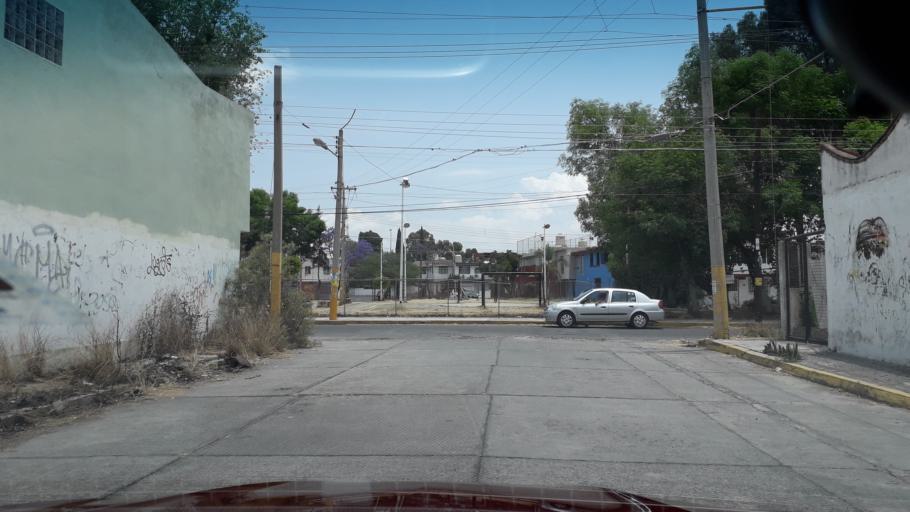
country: MX
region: Puebla
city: Tlazcalancingo
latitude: 18.9960
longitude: -98.2410
